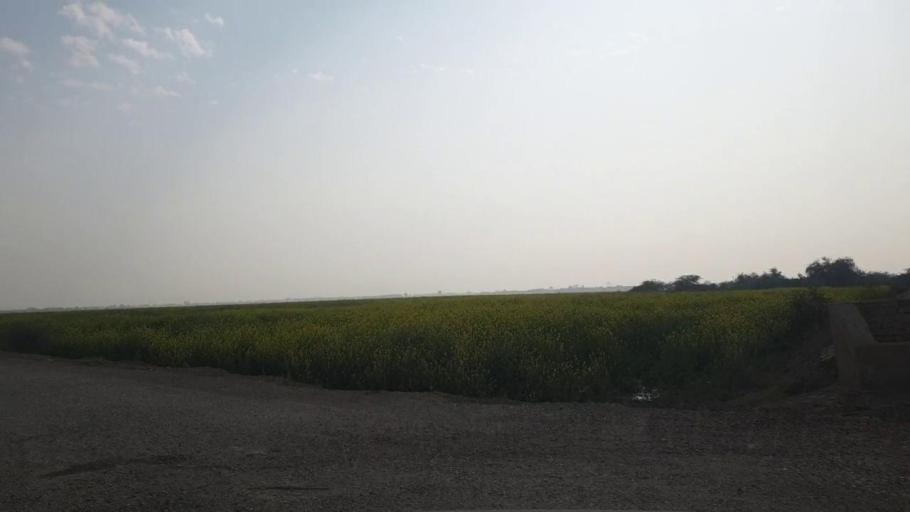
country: PK
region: Sindh
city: Hala
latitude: 25.7652
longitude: 68.4153
